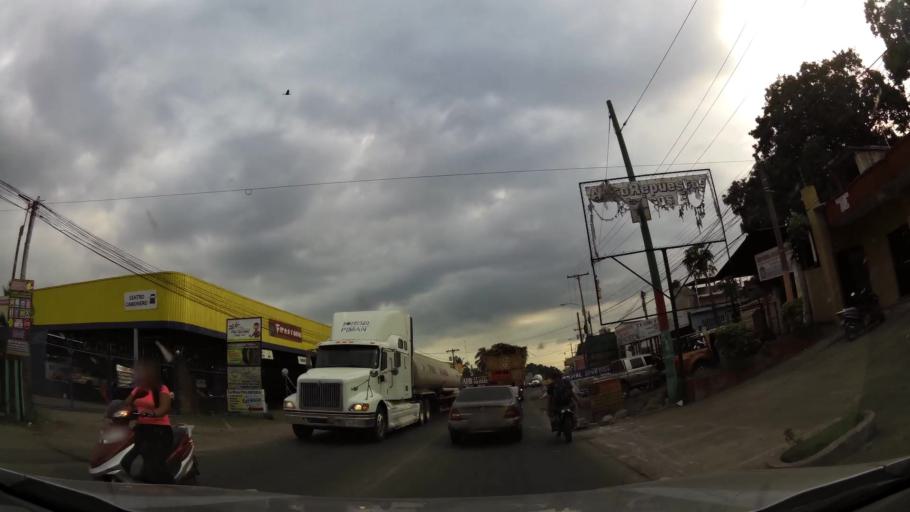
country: GT
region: Escuintla
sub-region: Municipio de Escuintla
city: Escuintla
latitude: 14.3015
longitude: -90.7810
